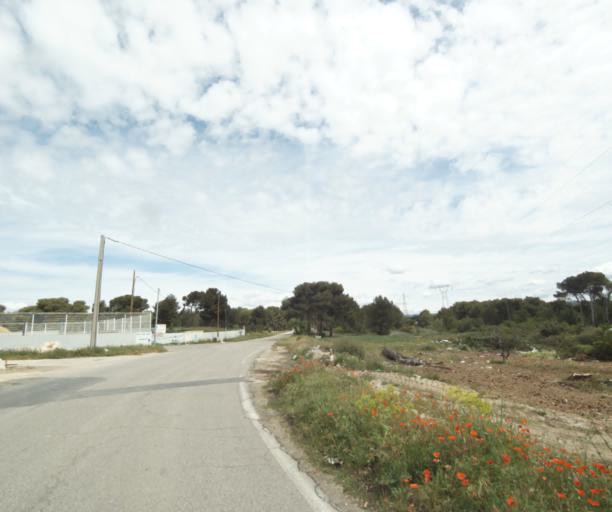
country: FR
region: Provence-Alpes-Cote d'Azur
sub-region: Departement des Bouches-du-Rhone
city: Rognac
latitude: 43.4972
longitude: 5.2044
